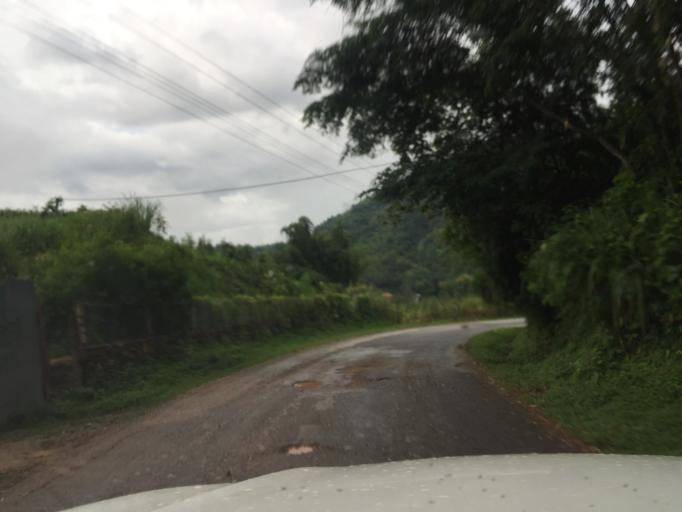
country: LA
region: Oudomxai
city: Muang La
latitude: 20.8745
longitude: 102.1429
